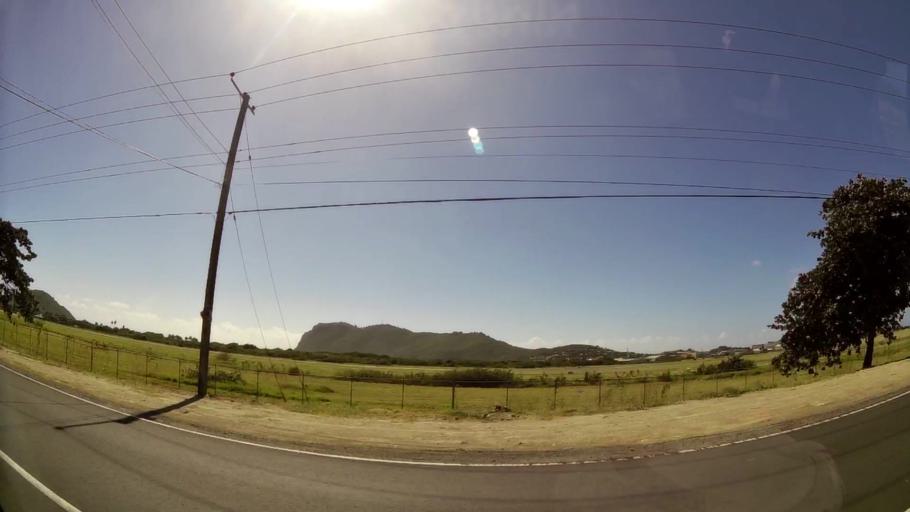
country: LC
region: Vieux-Fort
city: Vieux Fort
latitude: 13.7357
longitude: -60.9444
